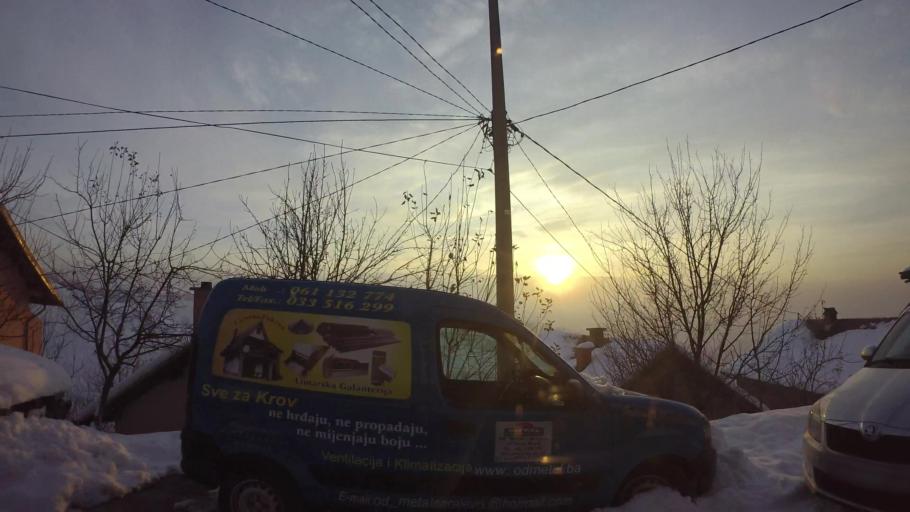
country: BA
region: Federation of Bosnia and Herzegovina
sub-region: Kanton Sarajevo
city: Sarajevo
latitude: 43.8390
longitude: 18.3561
